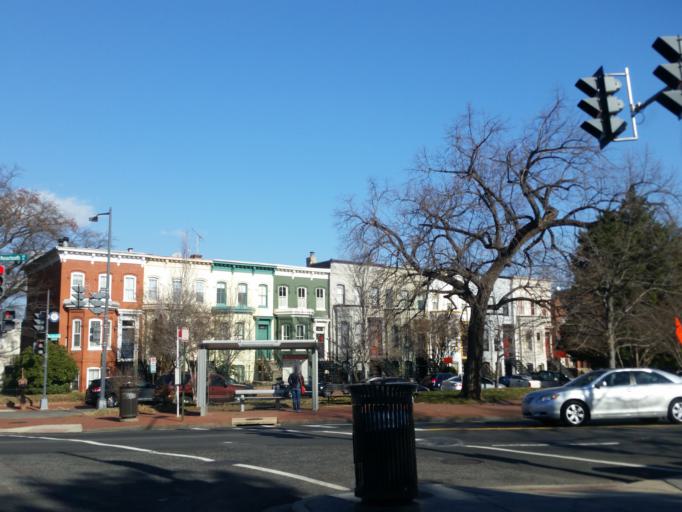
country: US
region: Washington, D.C.
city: Washington, D.C.
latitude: 38.8944
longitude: -77.0020
